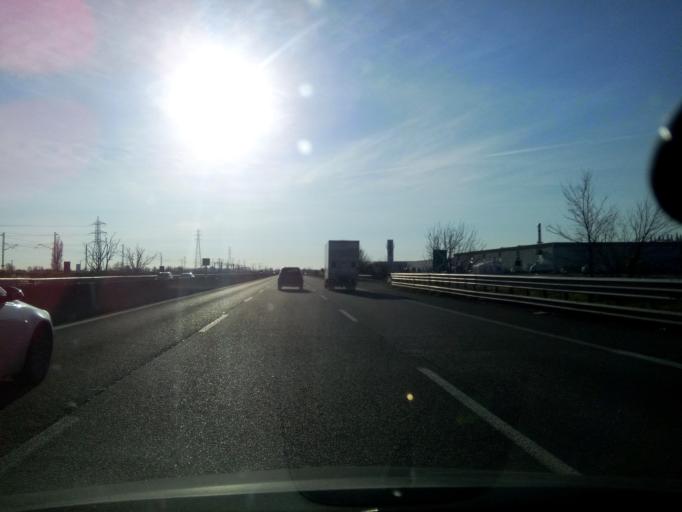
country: IT
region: Emilia-Romagna
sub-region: Provincia di Parma
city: Baganzola
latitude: 44.8530
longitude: 10.2844
